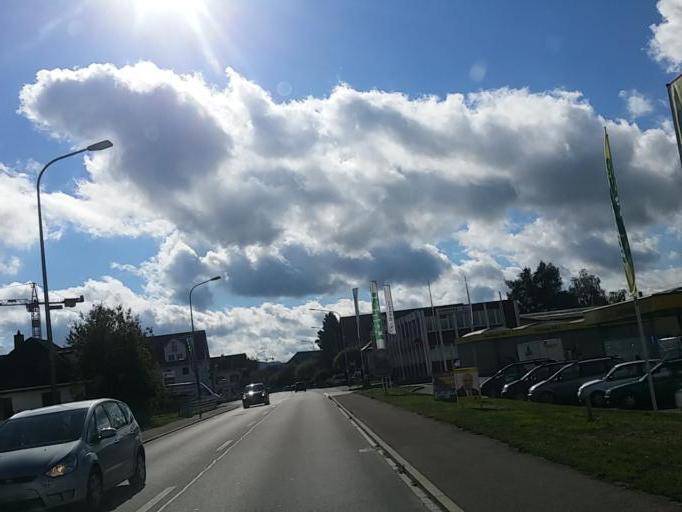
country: CH
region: Bern
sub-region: Oberaargau
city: Herzogenbuchsee
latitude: 47.1960
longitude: 7.6996
